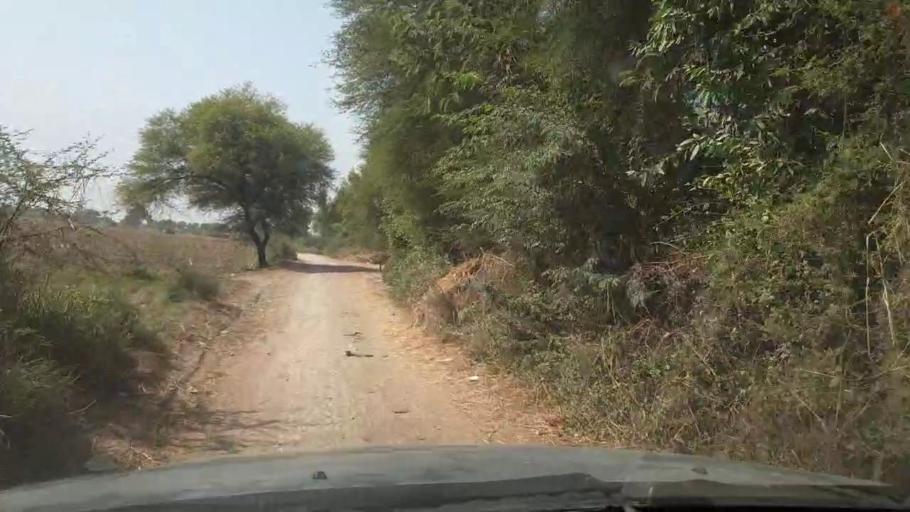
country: PK
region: Sindh
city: Bulri
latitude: 24.8725
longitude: 68.3170
